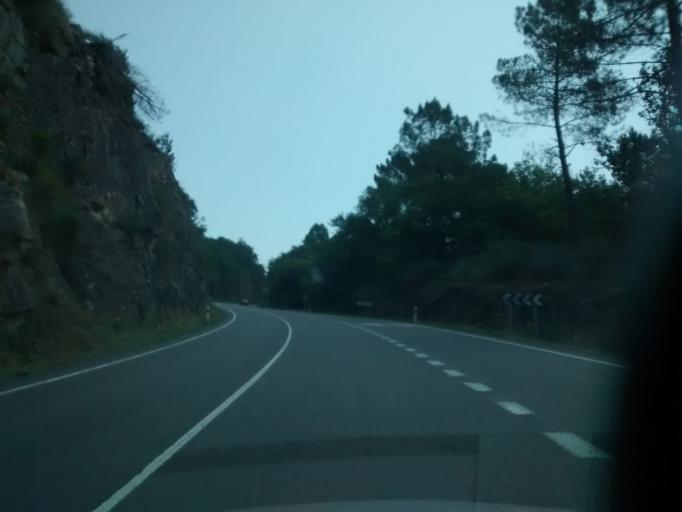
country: ES
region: Galicia
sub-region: Provincia de Ourense
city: O Carballino
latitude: 42.4253
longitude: -8.1015
